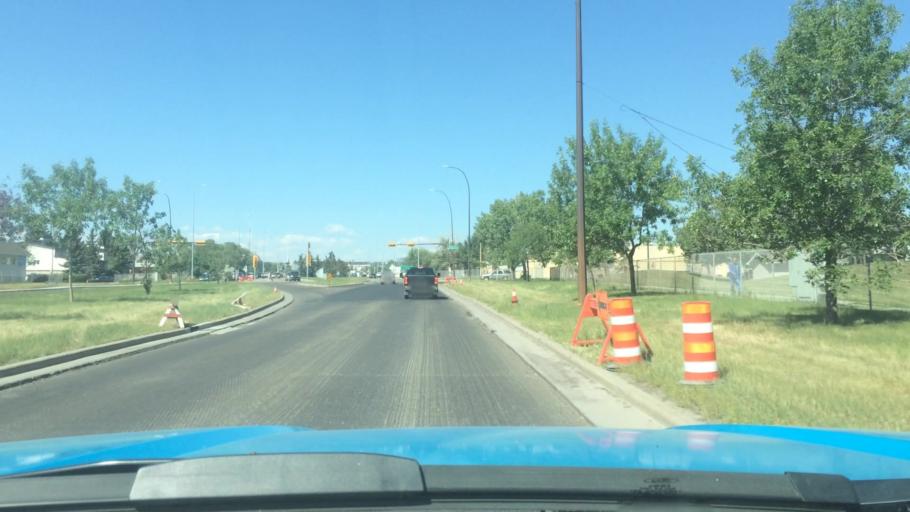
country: CA
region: Alberta
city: Calgary
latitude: 51.0529
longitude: -113.9750
